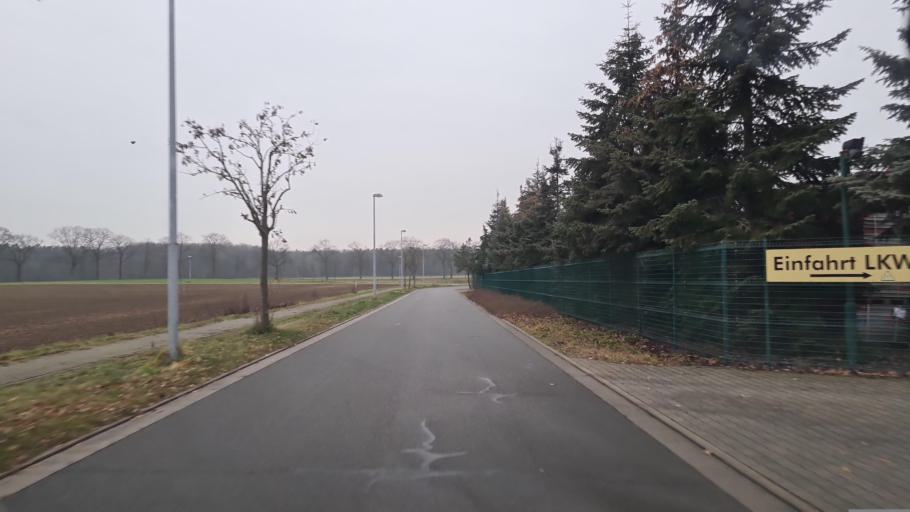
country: DE
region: Brandenburg
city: Werben
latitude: 51.7613
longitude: 14.1586
